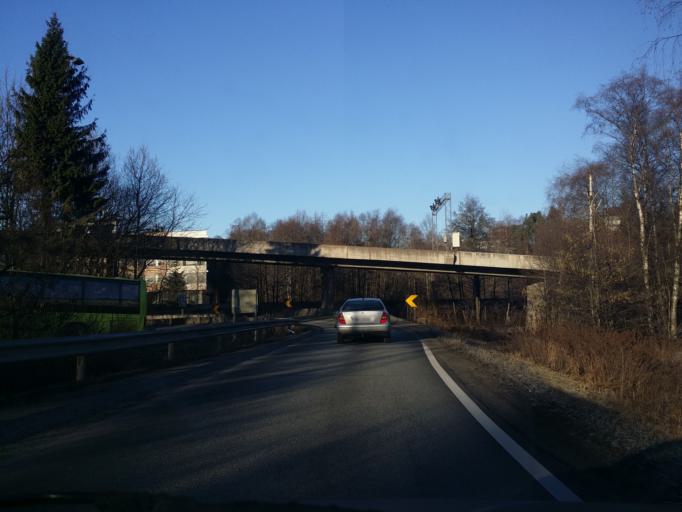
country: NO
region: Akershus
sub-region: Baerum
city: Lysaker
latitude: 59.9106
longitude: 10.6286
